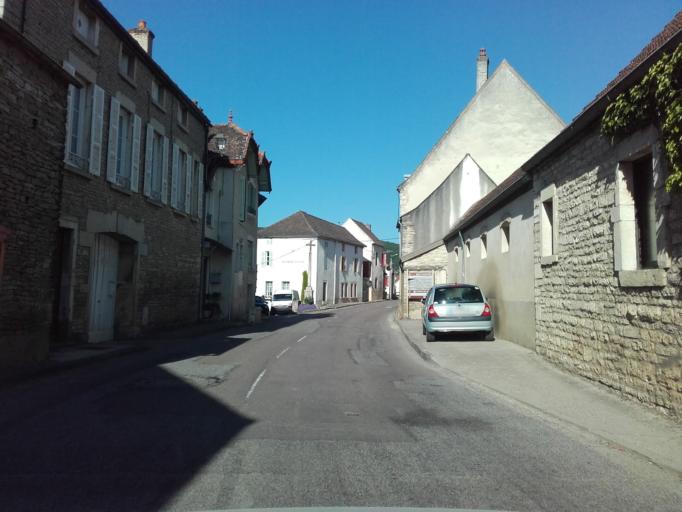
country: FR
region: Bourgogne
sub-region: Departement de la Cote-d'Or
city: Meursault
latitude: 46.9869
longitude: 4.7504
